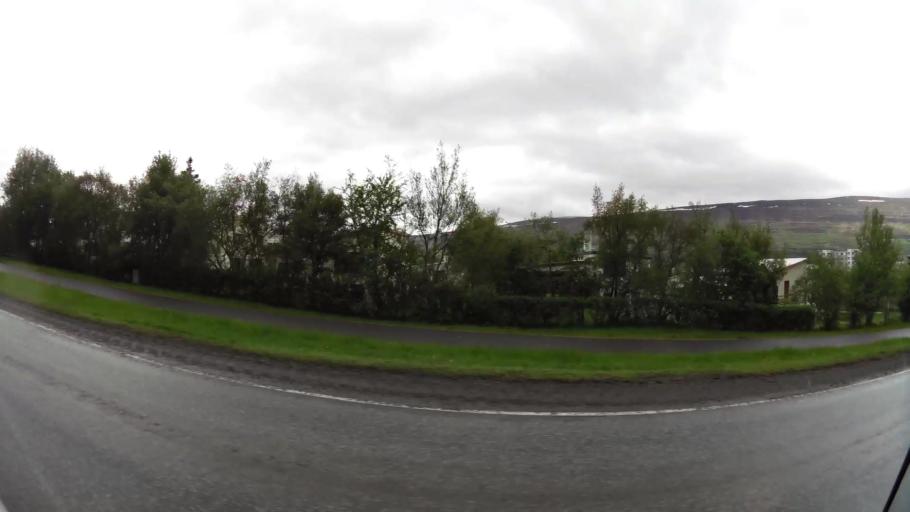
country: IS
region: Northeast
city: Akureyri
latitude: 65.6928
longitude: -18.1127
